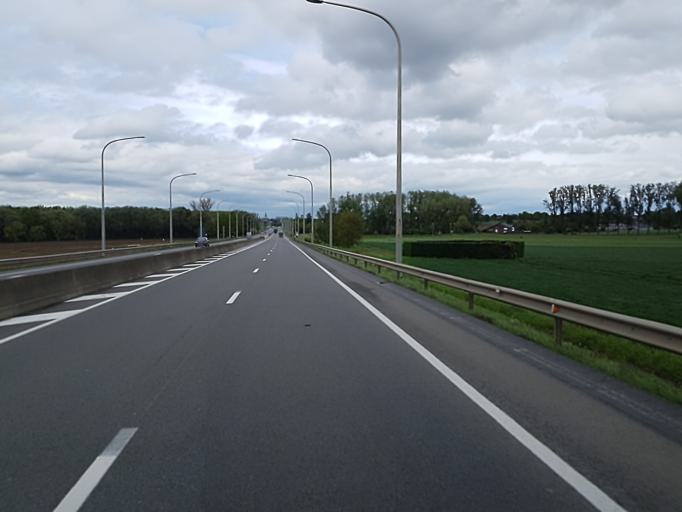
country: BE
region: Flanders
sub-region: Provincie Vlaams-Brabant
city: Tienen
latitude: 50.7835
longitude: 4.9231
